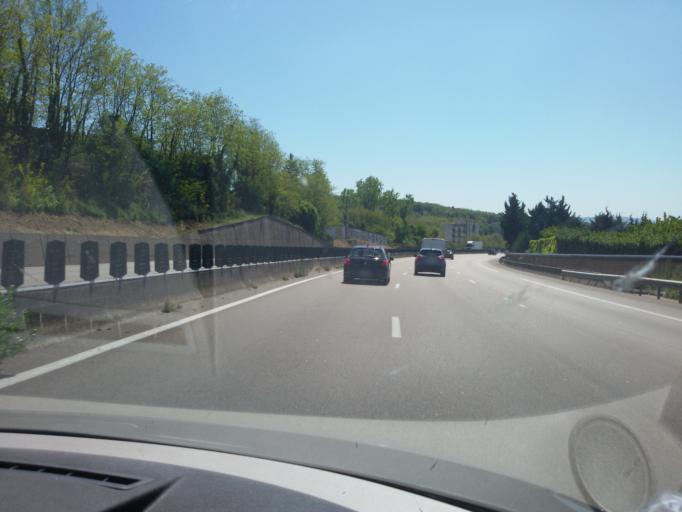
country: FR
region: Rhone-Alpes
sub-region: Departement de l'Isere
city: Roussillon
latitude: 45.3715
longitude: 4.8076
